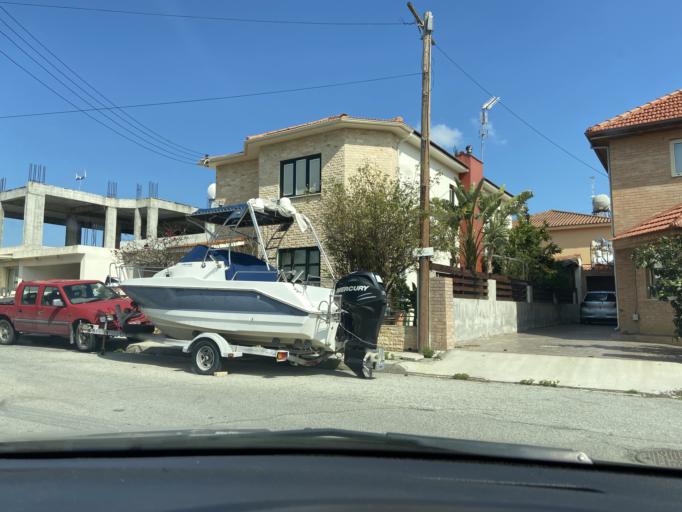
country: CY
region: Lefkosia
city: Dali
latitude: 35.0219
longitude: 33.3889
